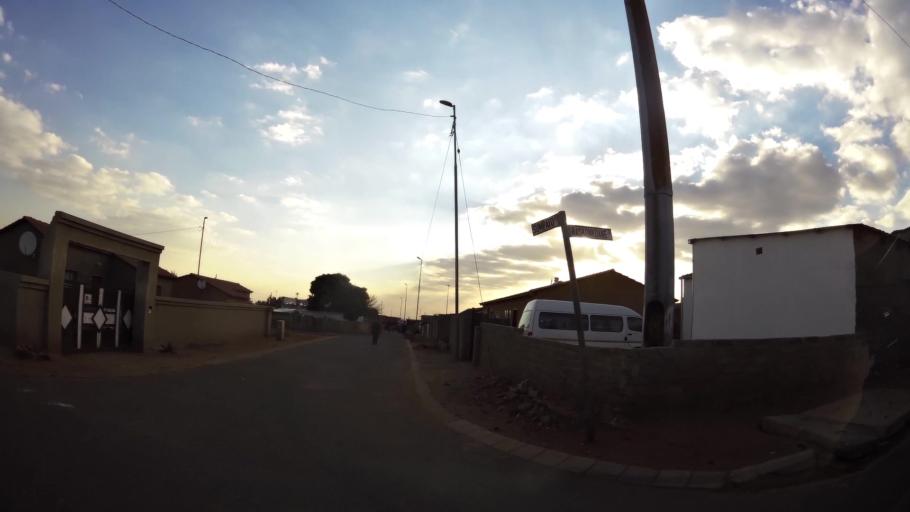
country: ZA
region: Gauteng
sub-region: West Rand District Municipality
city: Krugersdorp
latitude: -26.0784
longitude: 27.7593
